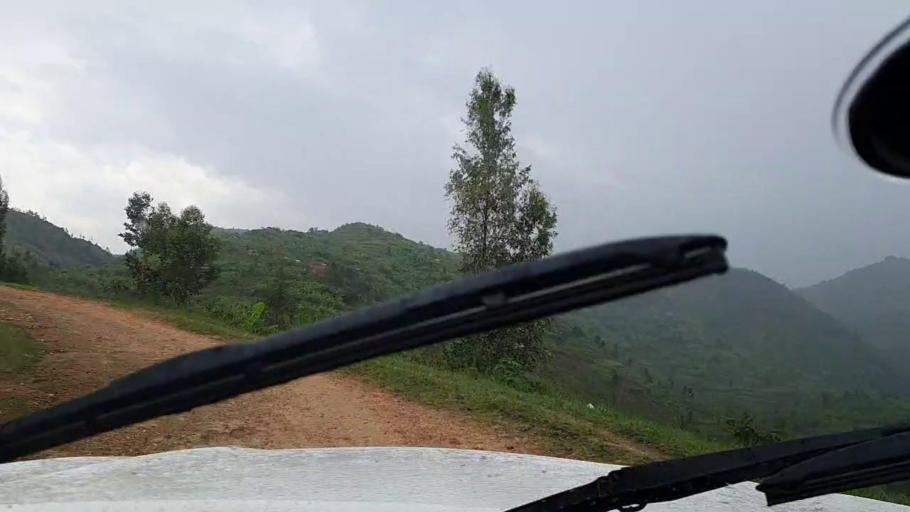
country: RW
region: Western Province
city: Kibuye
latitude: -2.0797
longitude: 29.4456
